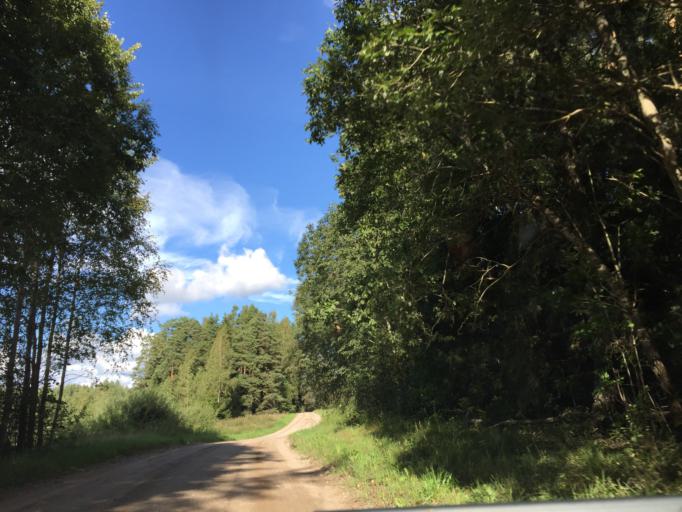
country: LV
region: Kuldigas Rajons
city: Kuldiga
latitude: 57.0030
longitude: 21.7750
